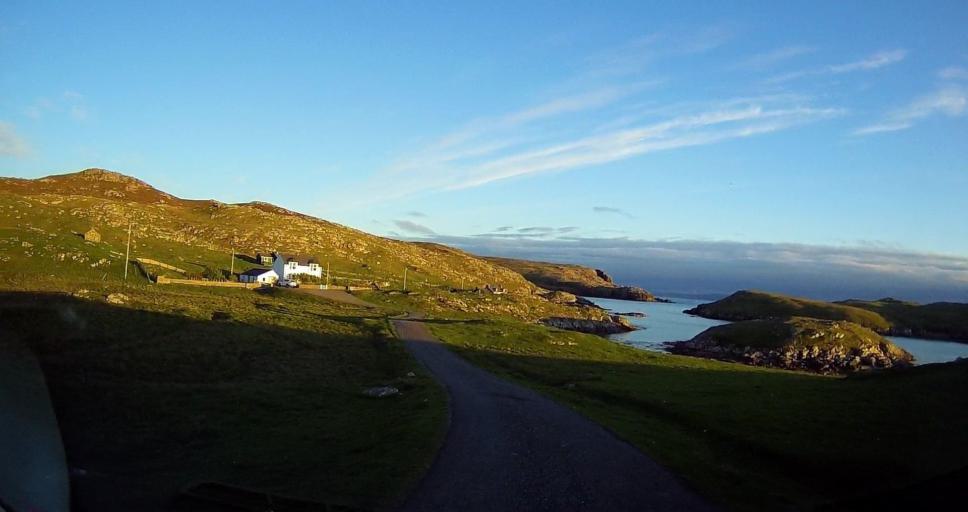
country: GB
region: Scotland
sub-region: Shetland Islands
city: Lerwick
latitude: 60.4426
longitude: -1.4466
